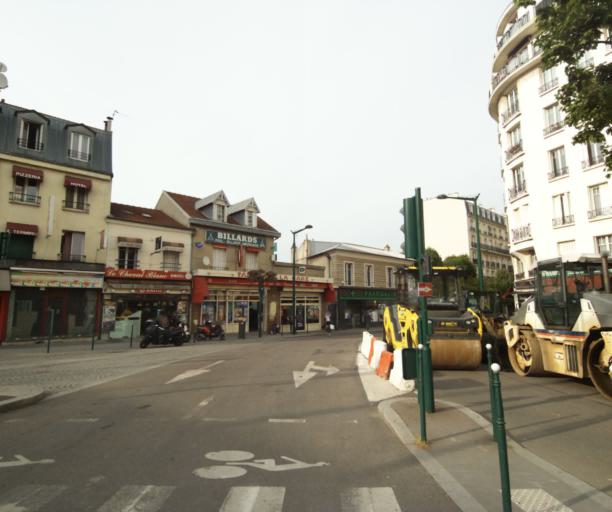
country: FR
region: Ile-de-France
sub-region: Departement des Hauts-de-Seine
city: Clichy
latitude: 48.8833
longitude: 2.3051
